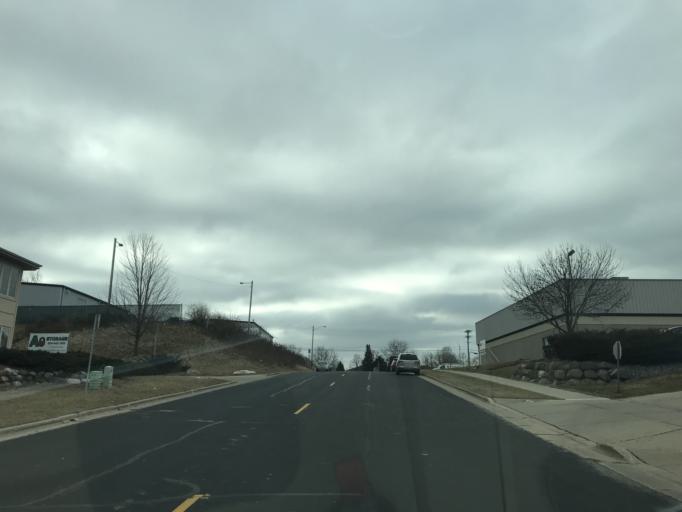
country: US
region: Wisconsin
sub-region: Dane County
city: Monona
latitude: 43.1080
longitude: -89.3100
